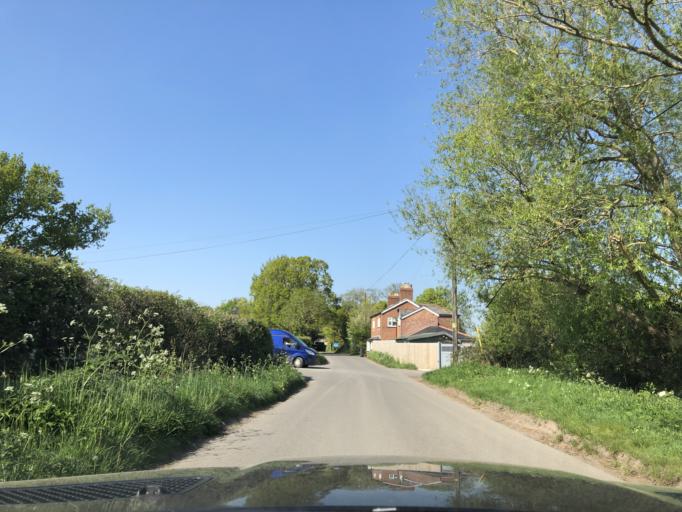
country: GB
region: England
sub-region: Warwickshire
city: Warwick
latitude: 52.2860
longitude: -1.6229
